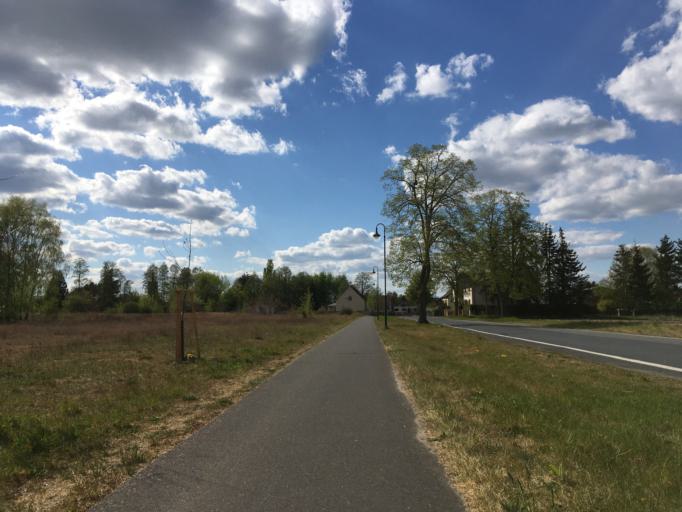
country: DE
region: Brandenburg
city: Wandlitz
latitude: 52.7773
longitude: 13.4440
